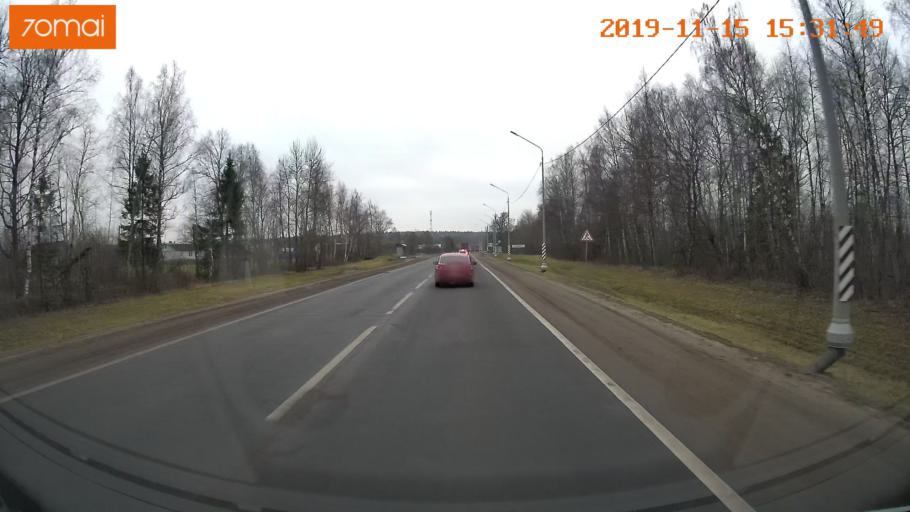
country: RU
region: Jaroslavl
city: Danilov
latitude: 58.0961
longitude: 40.1048
